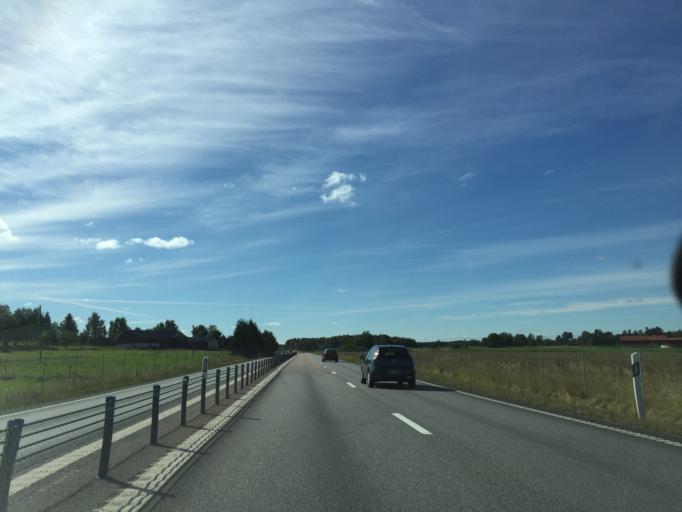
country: SE
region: Vaestmanland
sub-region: Kopings Kommun
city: Koping
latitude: 59.5691
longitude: 16.0872
